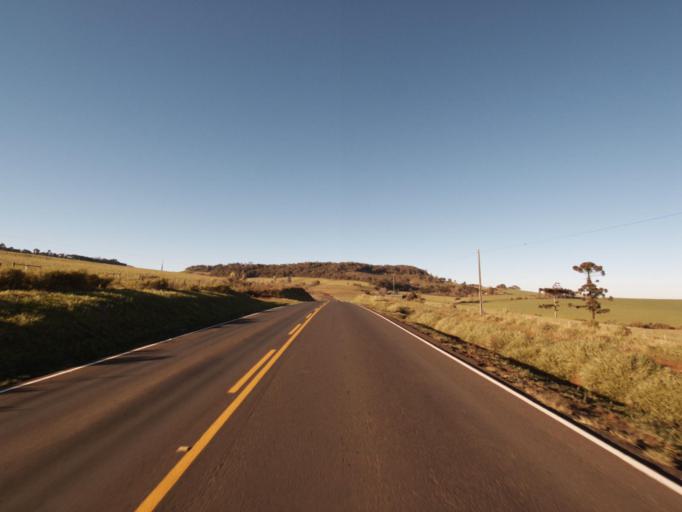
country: AR
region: Misiones
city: Bernardo de Irigoyen
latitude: -26.3496
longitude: -53.5451
